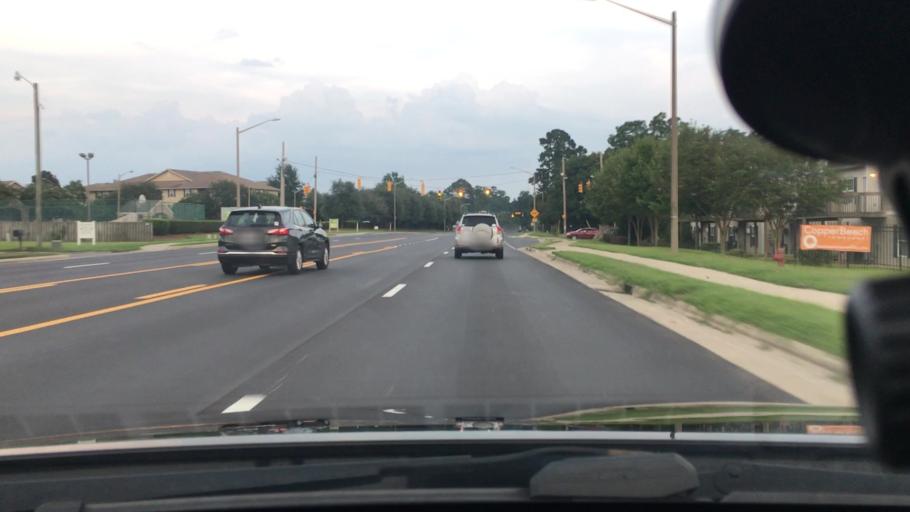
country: US
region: North Carolina
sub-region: Pitt County
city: Greenville
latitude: 35.5986
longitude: -77.3296
